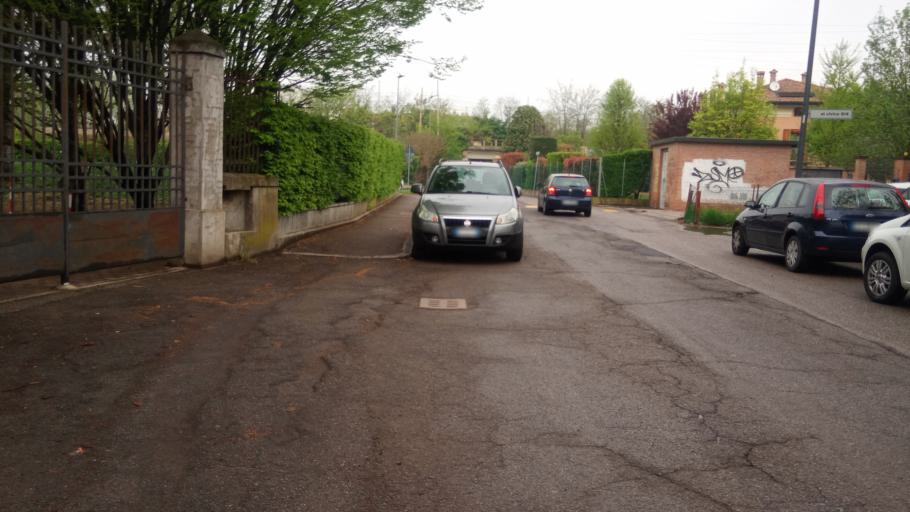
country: IT
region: Emilia-Romagna
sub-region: Provincia di Bologna
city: Bologna
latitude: 44.5207
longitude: 11.3401
